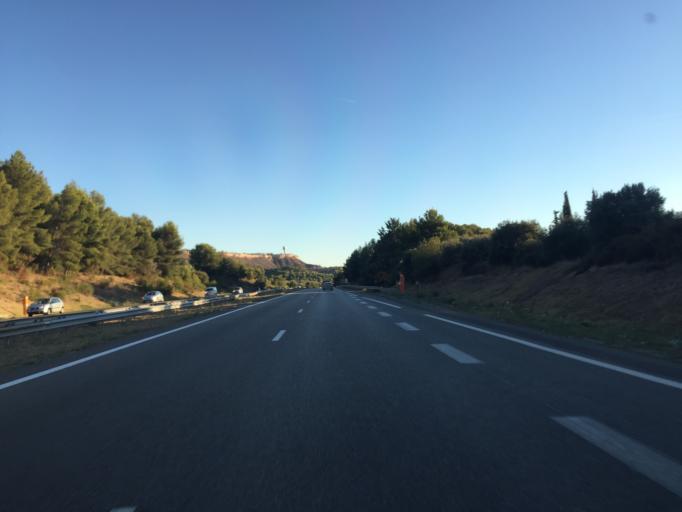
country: FR
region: Provence-Alpes-Cote d'Azur
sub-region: Departement des Bouches-du-Rhone
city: Rognac
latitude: 43.4917
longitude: 5.2399
